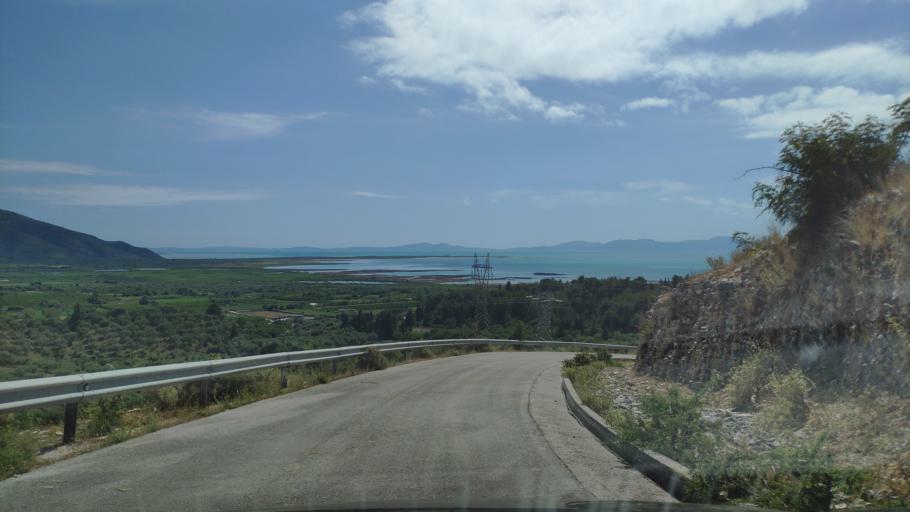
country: AL
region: Vlore
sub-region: Rrethi i Sarandes
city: Konispol
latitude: 39.6247
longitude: 20.2053
